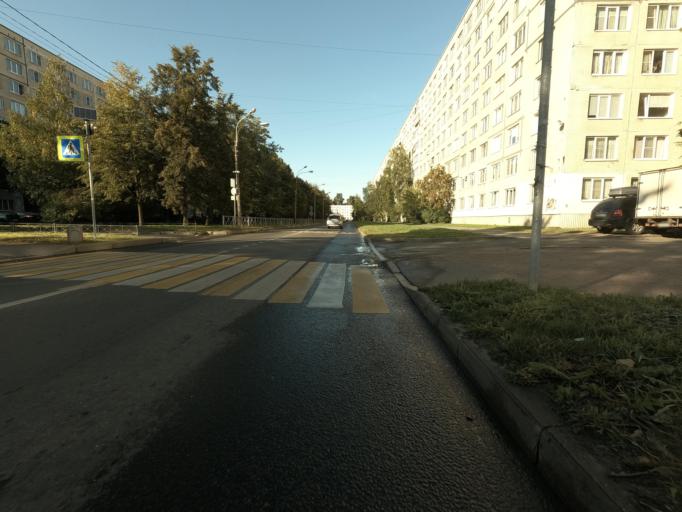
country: RU
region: St.-Petersburg
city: Kolpino
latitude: 59.7392
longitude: 30.5690
